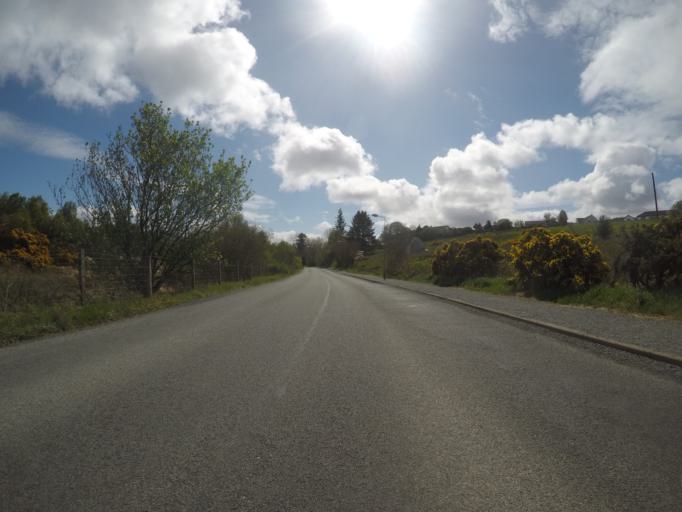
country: GB
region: Scotland
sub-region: Highland
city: Portree
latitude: 57.4192
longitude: -6.1928
